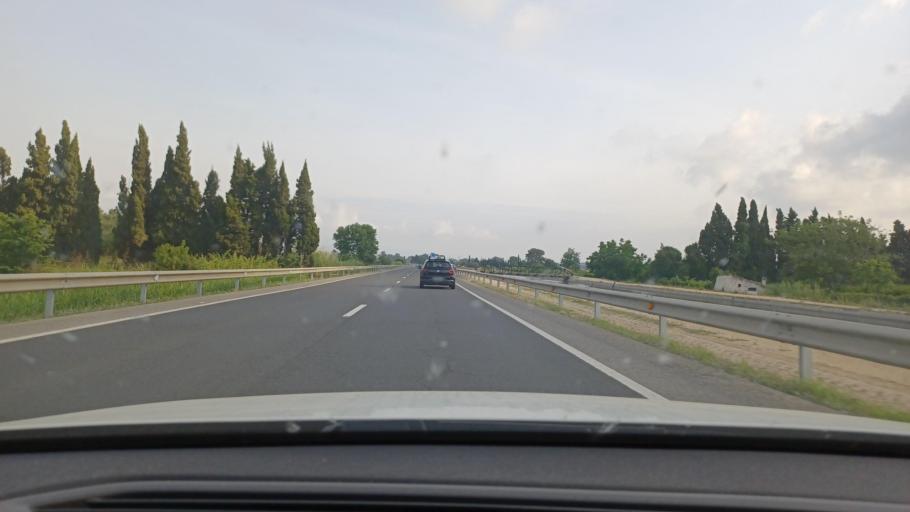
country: ES
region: Catalonia
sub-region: Provincia de Tarragona
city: Tortosa
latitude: 40.7658
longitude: 0.5320
